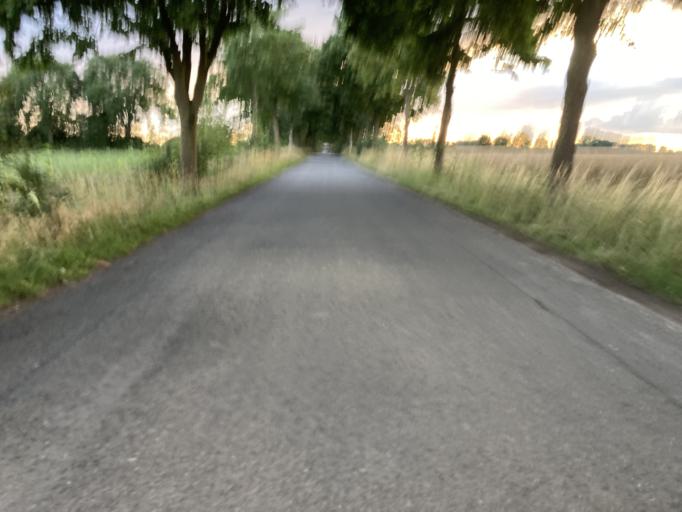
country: DE
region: Lower Saxony
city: Verden
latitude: 52.9280
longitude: 9.2095
